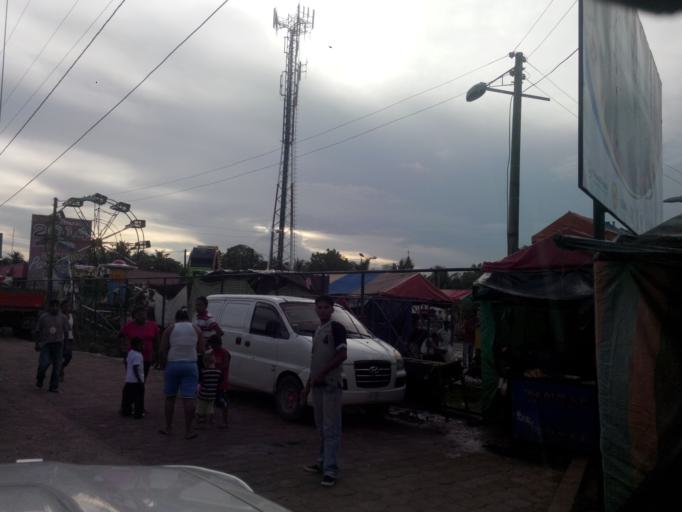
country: NI
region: Atlantico Norte (RAAN)
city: Puerto Cabezas
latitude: 14.0283
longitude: -83.3816
